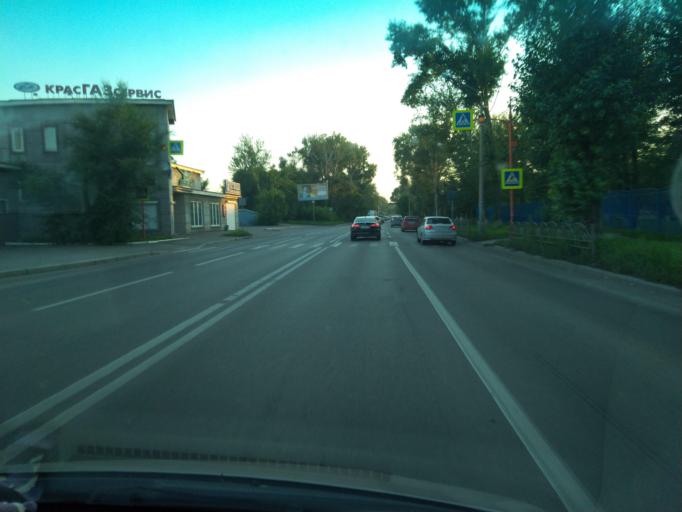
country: RU
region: Krasnoyarskiy
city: Krasnoyarsk
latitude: 55.9866
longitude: 92.8965
